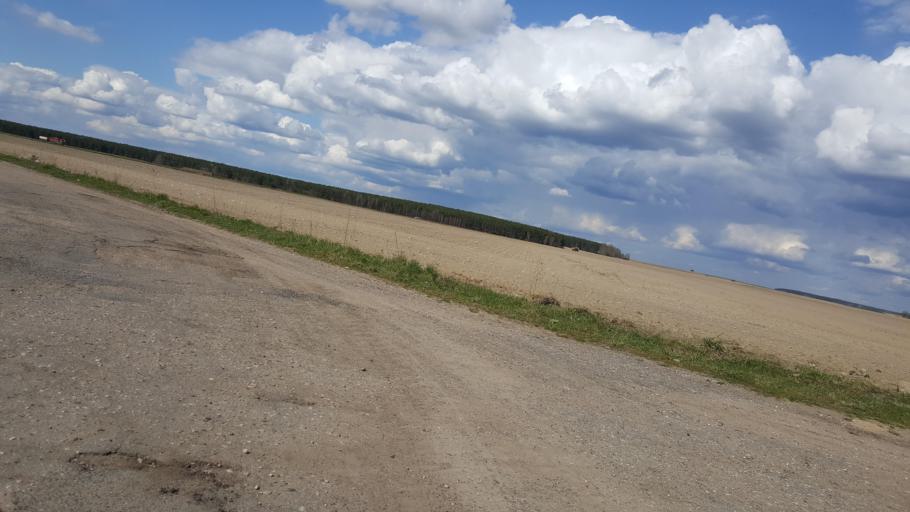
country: BY
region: Brest
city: Kamyanyets
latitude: 52.4101
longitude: 23.6425
